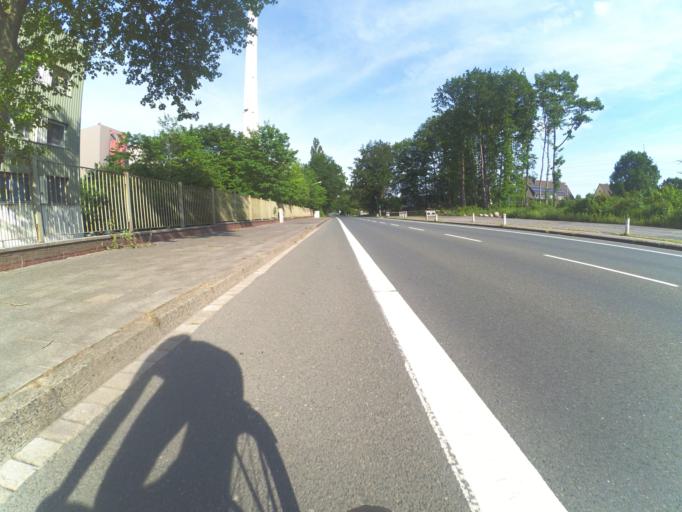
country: DE
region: North Rhine-Westphalia
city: Ibbenburen
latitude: 52.2859
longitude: 7.7413
